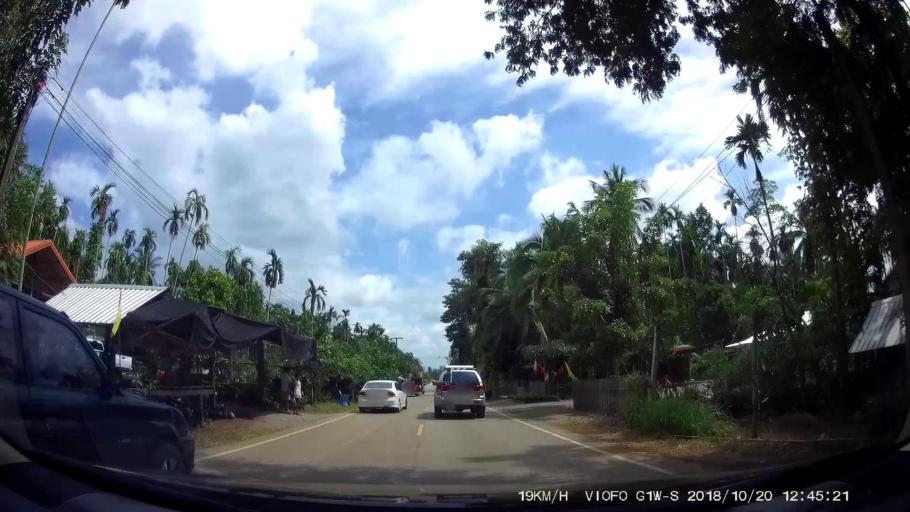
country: TH
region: Chaiyaphum
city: Khon San
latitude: 16.5367
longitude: 101.8736
